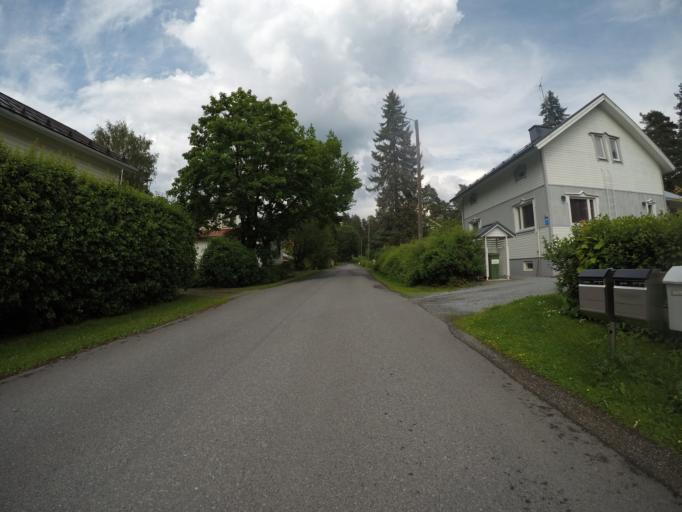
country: FI
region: Haeme
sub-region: Haemeenlinna
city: Haemeenlinna
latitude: 61.0116
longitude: 24.4741
